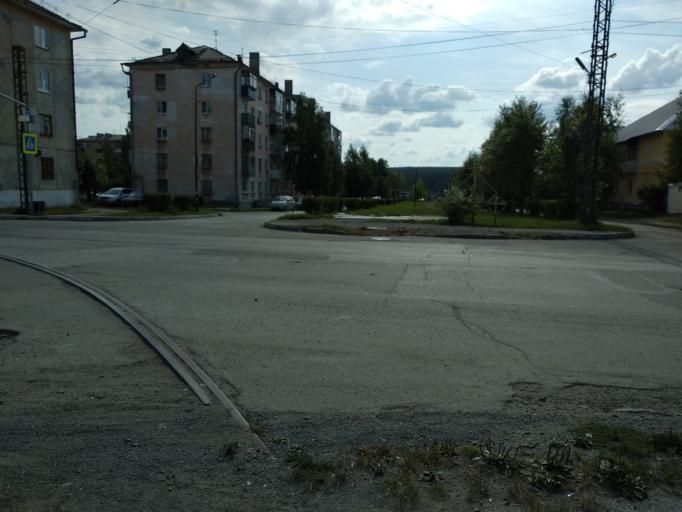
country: RU
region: Sverdlovsk
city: Krasnotur'insk
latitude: 59.7606
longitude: 60.1872
